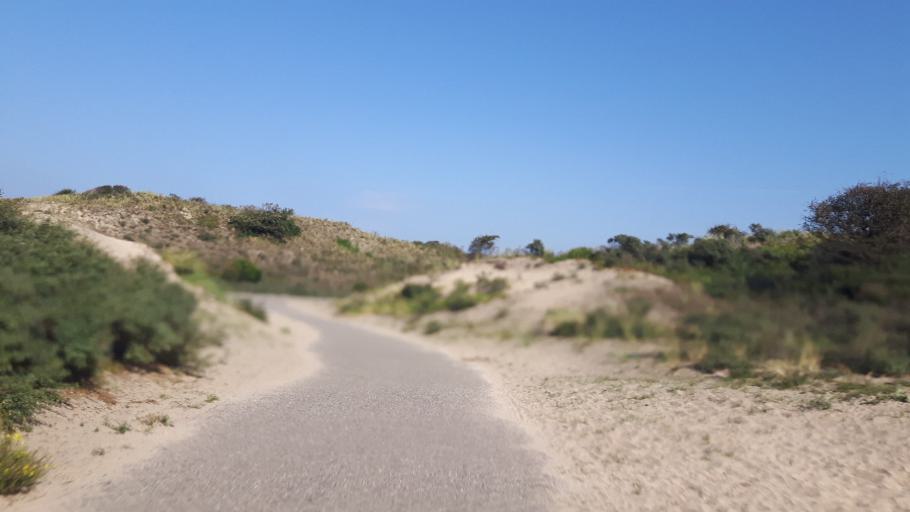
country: NL
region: North Holland
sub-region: Gemeente Zandvoort
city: Zandvoort
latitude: 52.3866
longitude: 4.5555
